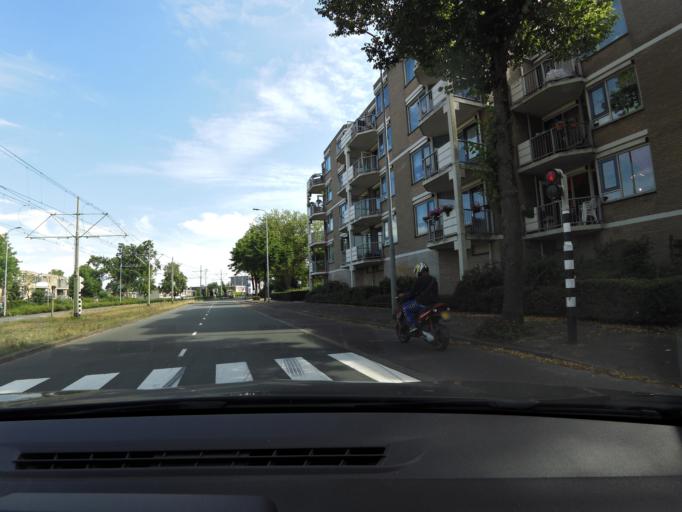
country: NL
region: South Holland
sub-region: Gemeente Delft
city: Delft
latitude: 52.0248
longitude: 4.3501
